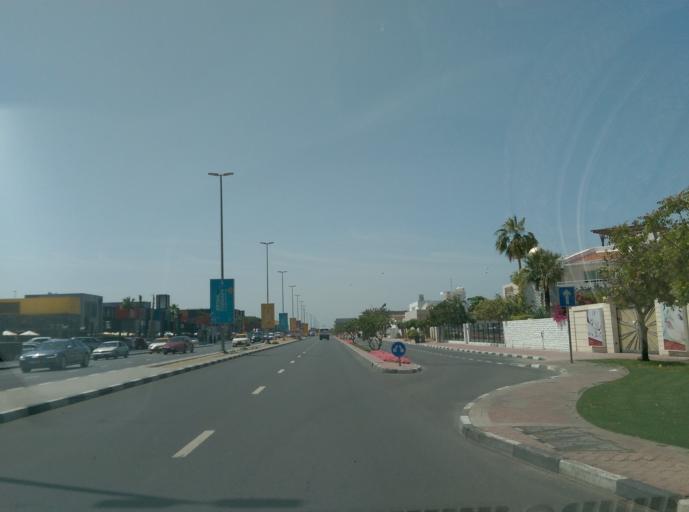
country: AE
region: Dubai
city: Dubai
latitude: 25.2010
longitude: 55.2495
